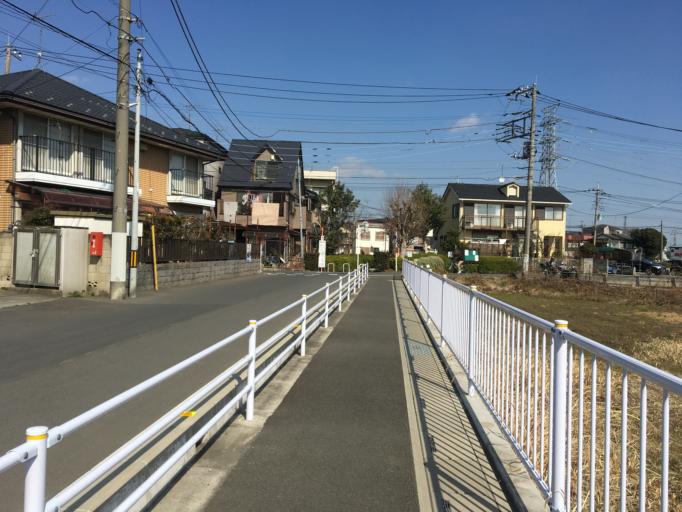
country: JP
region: Saitama
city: Shiki
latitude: 35.8411
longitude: 139.5717
